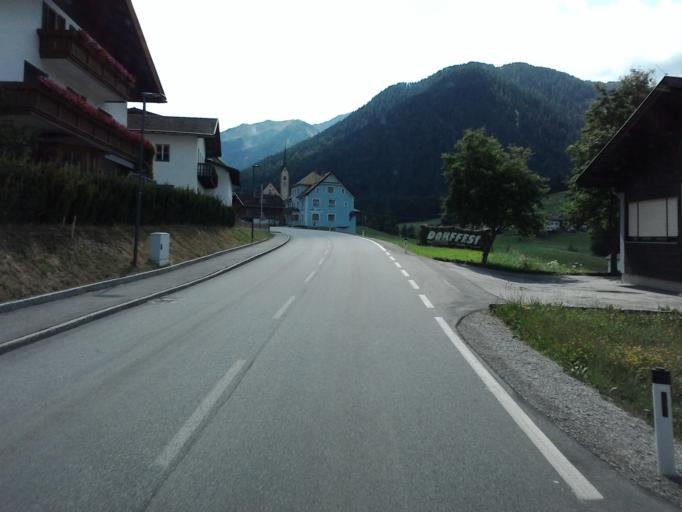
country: AT
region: Tyrol
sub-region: Politischer Bezirk Lienz
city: Kartitsch
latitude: 46.7273
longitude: 12.4950
